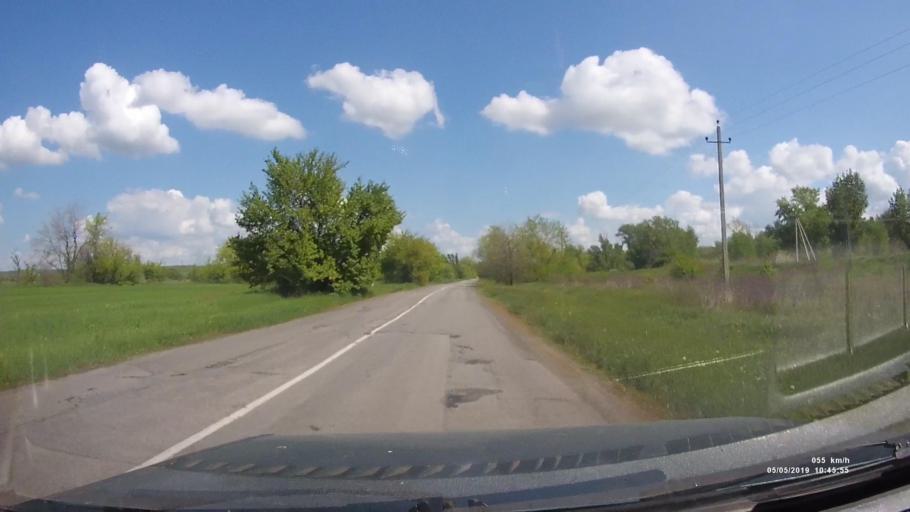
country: RU
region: Rostov
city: Ust'-Donetskiy
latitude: 47.6307
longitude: 40.8406
